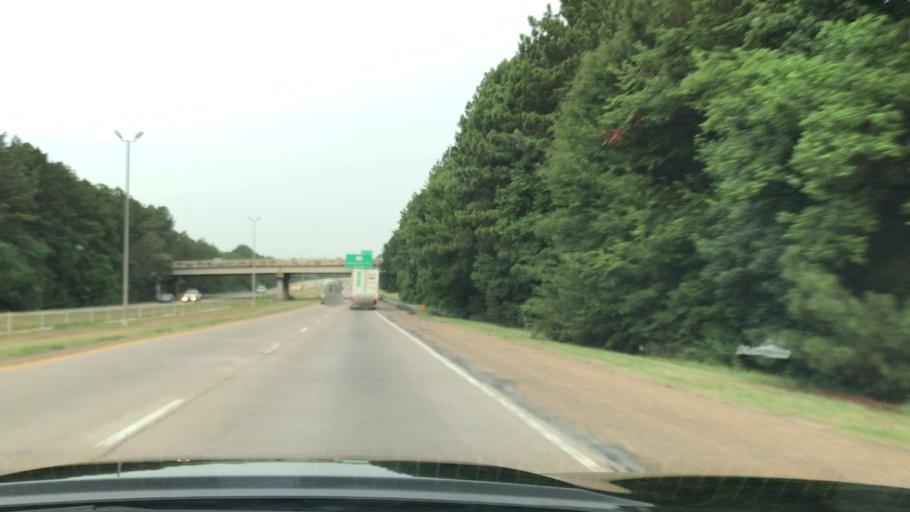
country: US
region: Louisiana
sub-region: Bossier Parish
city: Bossier City
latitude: 32.4189
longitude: -93.7786
